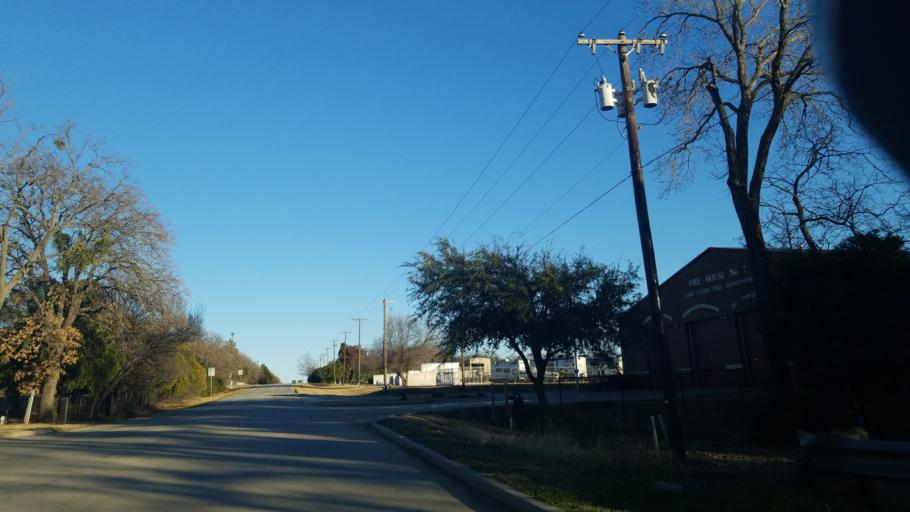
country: US
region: Texas
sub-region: Denton County
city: Corinth
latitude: 33.1631
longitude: -97.0667
